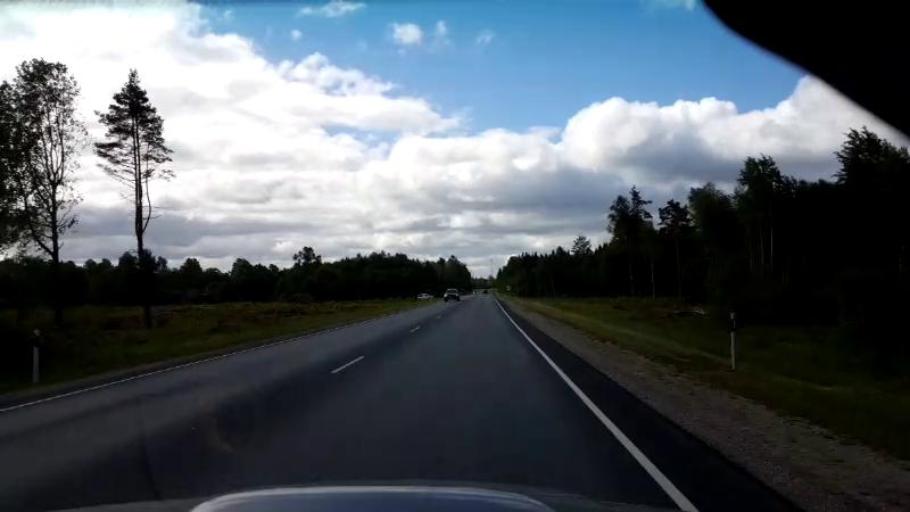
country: EE
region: Raplamaa
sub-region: Maerjamaa vald
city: Marjamaa
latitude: 59.0378
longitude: 24.4435
